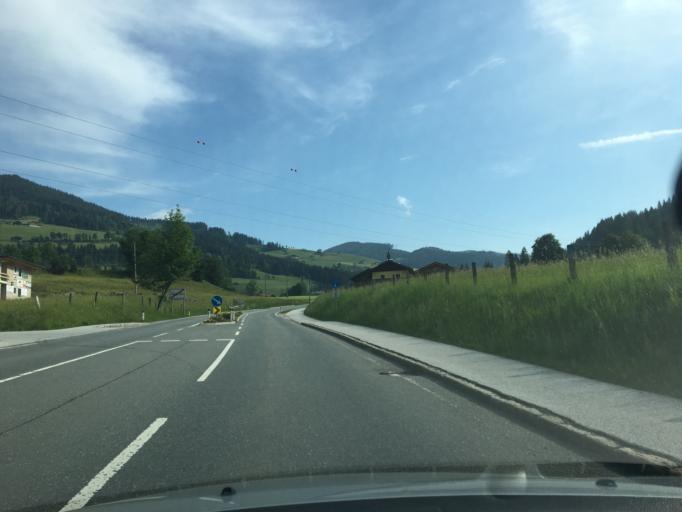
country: AT
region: Salzburg
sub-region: Politischer Bezirk Sankt Johann im Pongau
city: Wagrain
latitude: 47.3411
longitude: 13.3048
